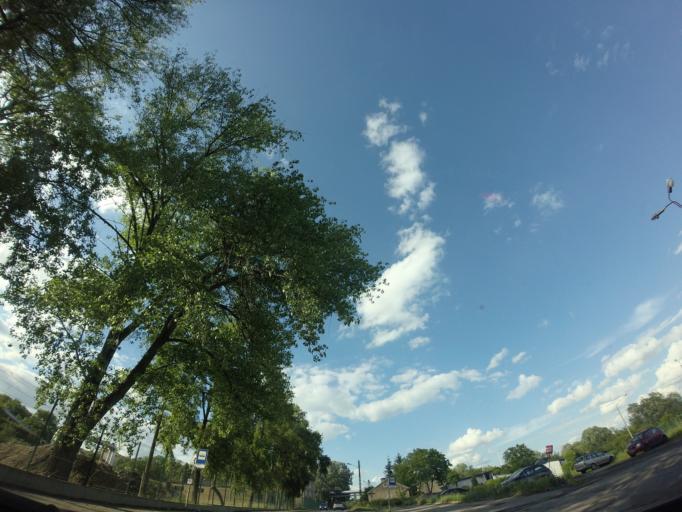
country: PL
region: West Pomeranian Voivodeship
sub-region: Szczecin
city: Szczecin
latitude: 53.3919
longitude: 14.5285
